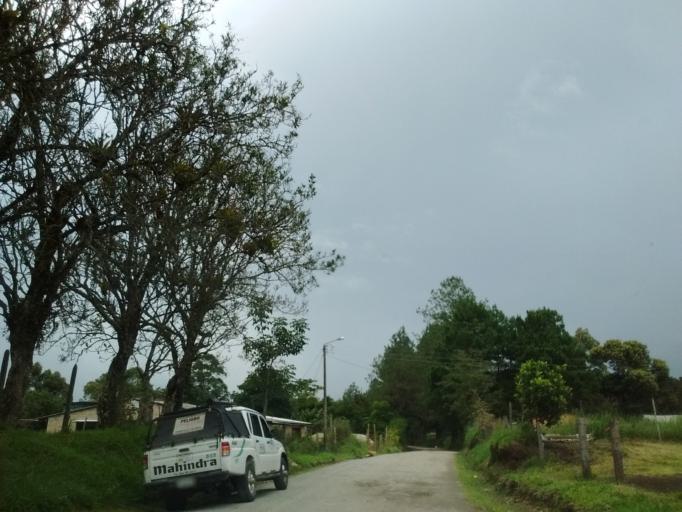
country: CO
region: Cauca
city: Cajibio
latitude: 2.5460
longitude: -76.6232
